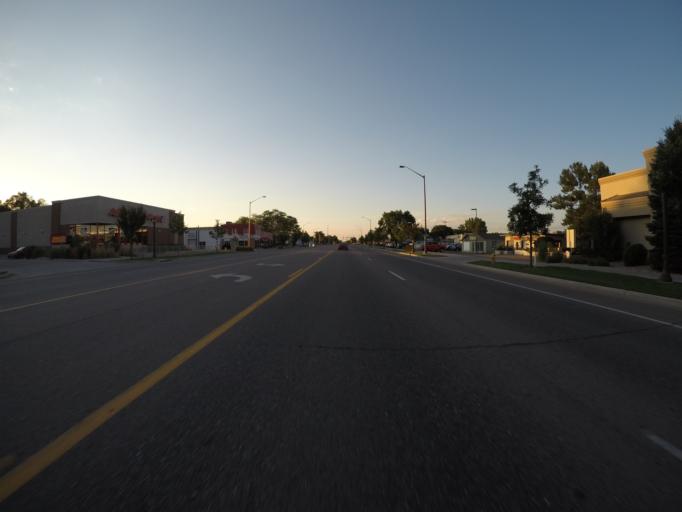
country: US
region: Colorado
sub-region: Larimer County
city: Fort Collins
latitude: 40.6006
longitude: -105.0766
